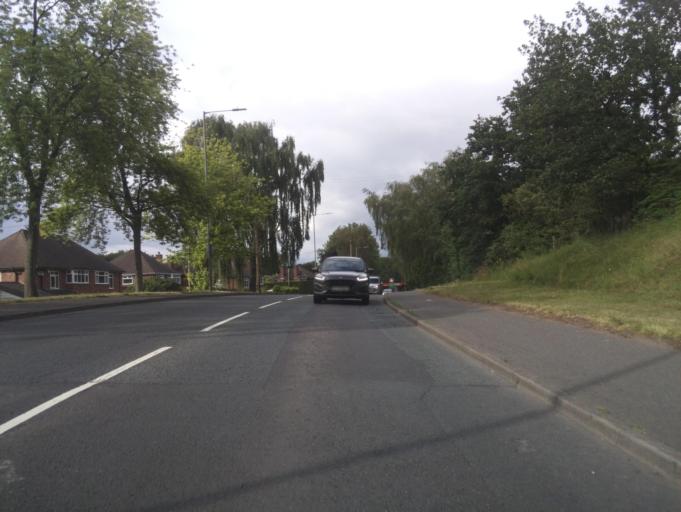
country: GB
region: England
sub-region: Dudley
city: Kingswinford
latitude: 52.5025
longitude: -2.1825
